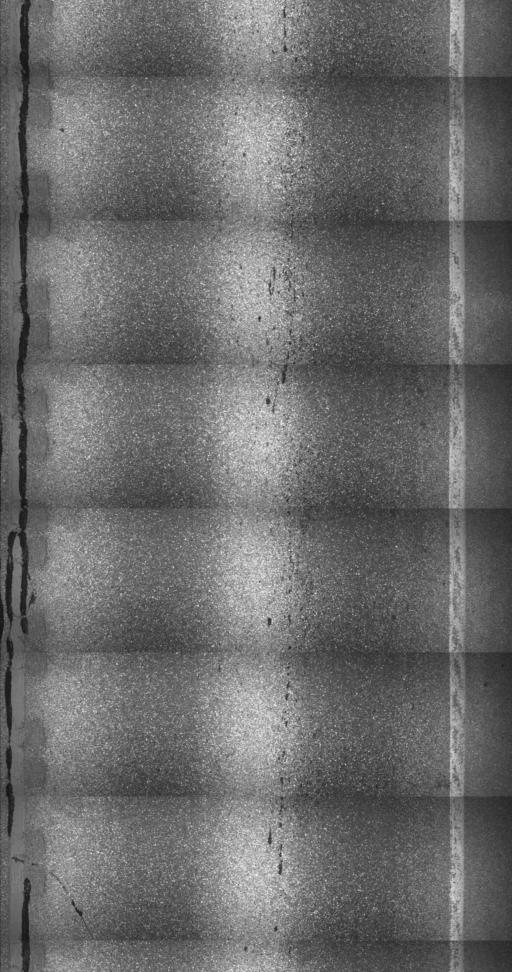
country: US
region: Vermont
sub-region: Franklin County
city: Enosburg Falls
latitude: 44.9109
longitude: -72.9032
